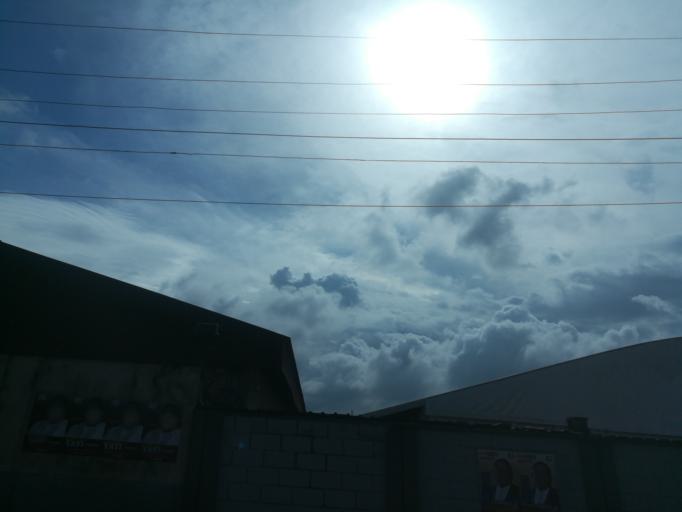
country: NG
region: Lagos
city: Agege
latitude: 6.6269
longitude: 3.3493
